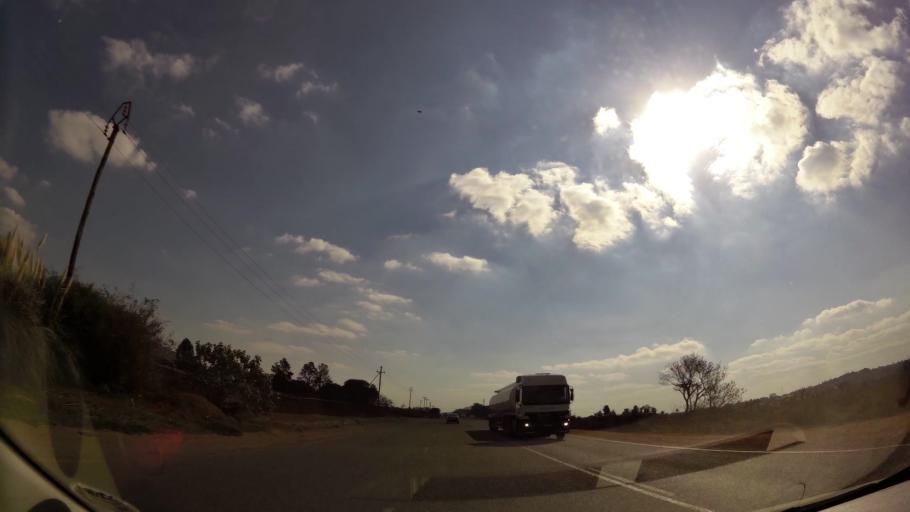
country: ZA
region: Gauteng
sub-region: West Rand District Municipality
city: Muldersdriseloop
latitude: -26.0466
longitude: 27.8004
